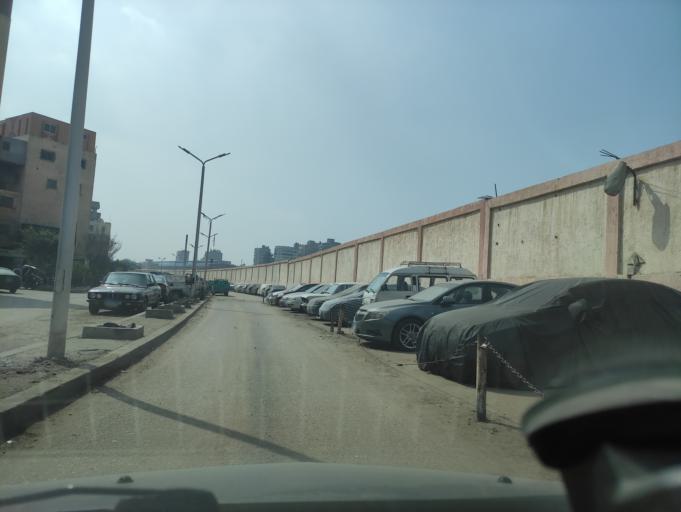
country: EG
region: Muhafazat al Qahirah
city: Cairo
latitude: 30.0782
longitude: 31.2572
